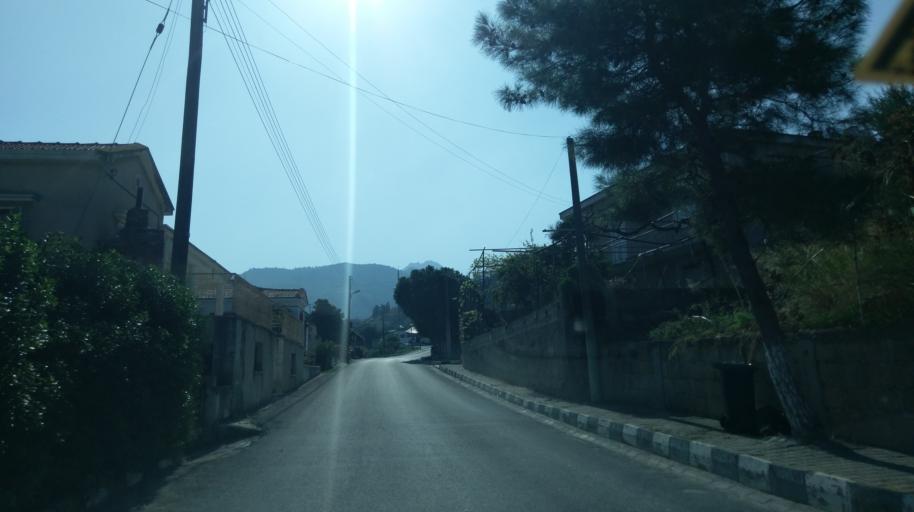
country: CY
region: Ammochostos
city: Lefkonoiko
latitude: 35.3805
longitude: 33.7519
